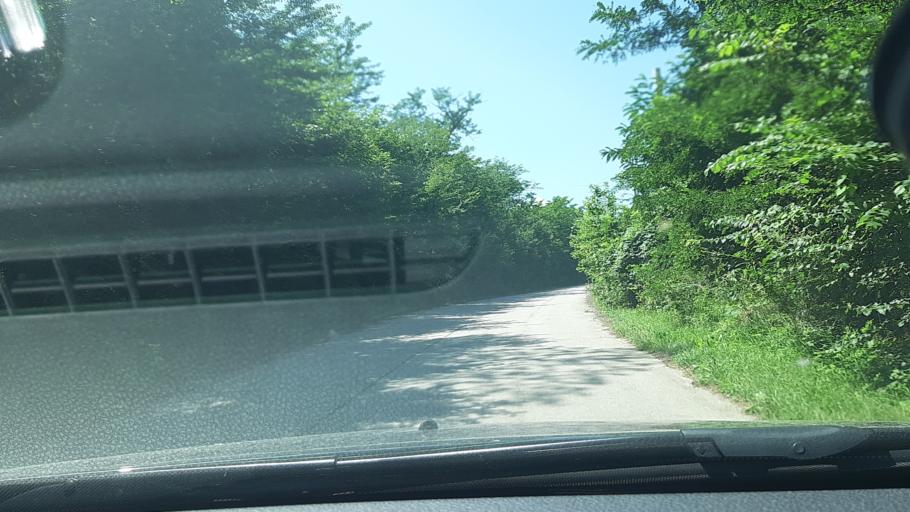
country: RO
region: Hunedoara
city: Bucium-Orlea
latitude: 45.5871
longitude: 22.9631
